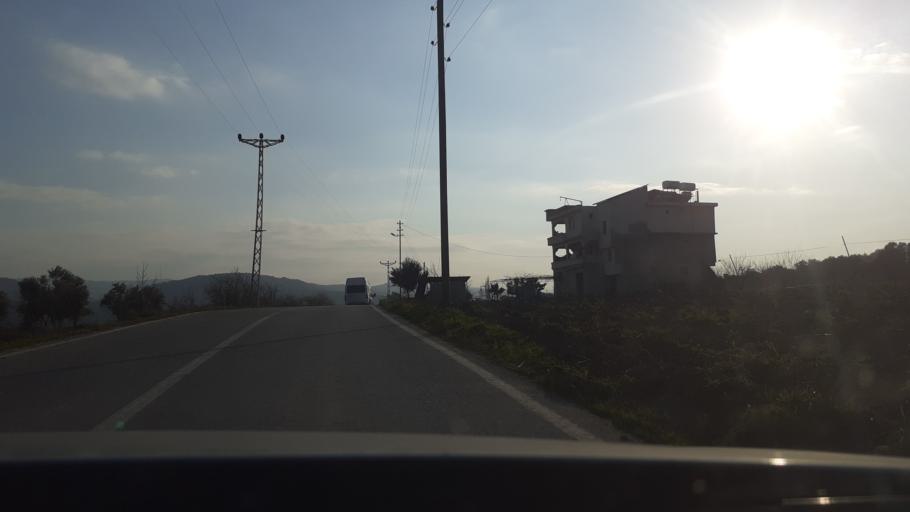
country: TR
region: Hatay
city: Boynuyogun
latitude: 36.1356
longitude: 36.3130
